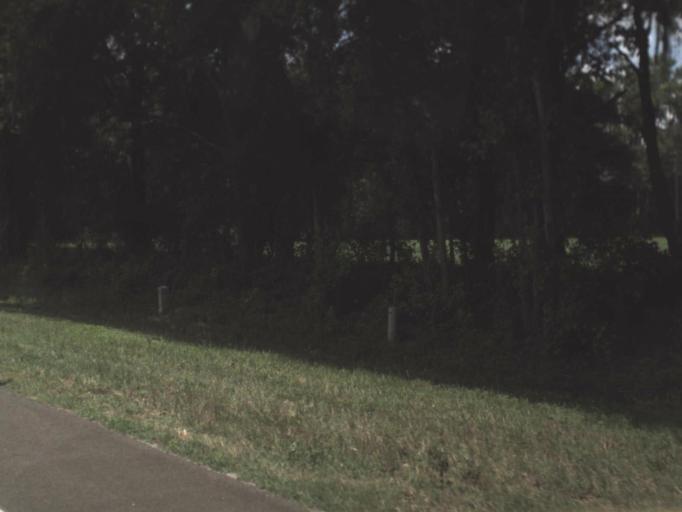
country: US
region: Florida
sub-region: Alachua County
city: Alachua
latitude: 29.7881
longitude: -82.3790
